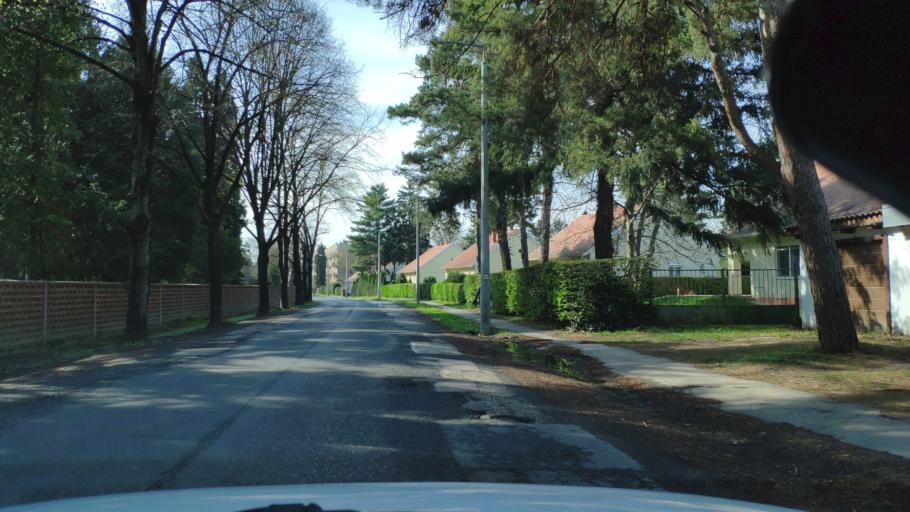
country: HU
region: Zala
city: Nagykanizsa
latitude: 46.4463
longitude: 16.9958
